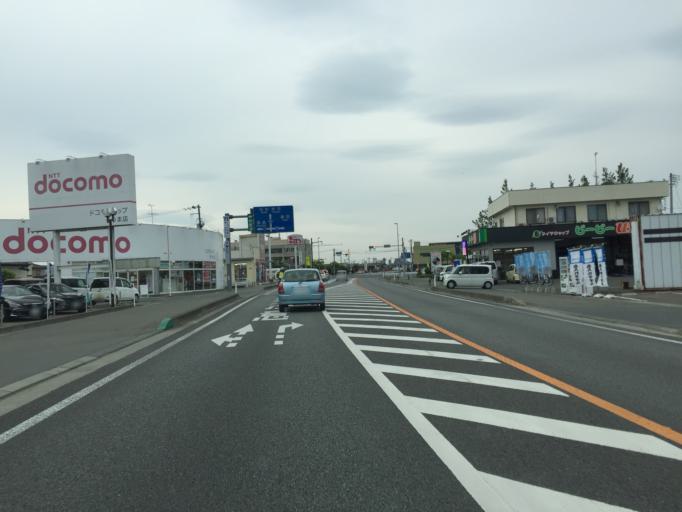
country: JP
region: Miyagi
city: Marumori
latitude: 37.7913
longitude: 140.9296
